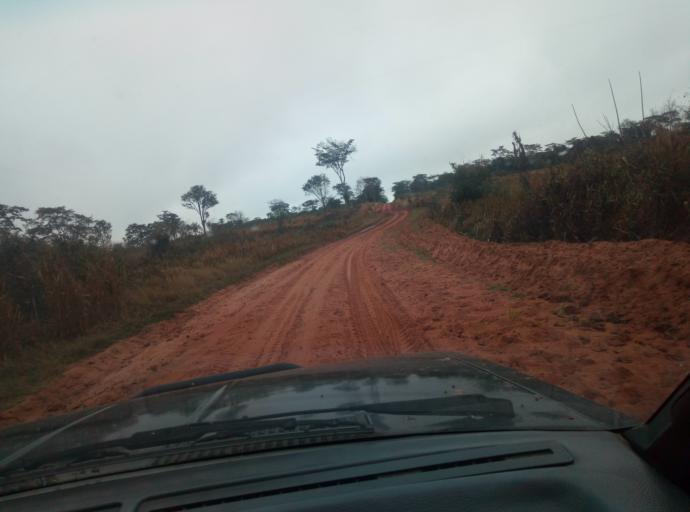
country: PY
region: Caaguazu
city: Carayao
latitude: -25.1926
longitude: -56.3358
